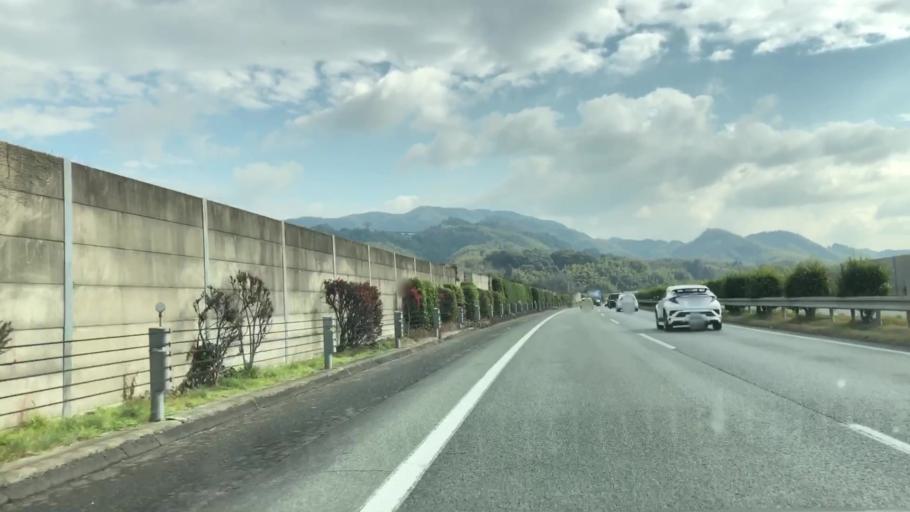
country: JP
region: Fukuoka
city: Setakamachi-takayanagi
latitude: 33.1163
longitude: 130.5274
